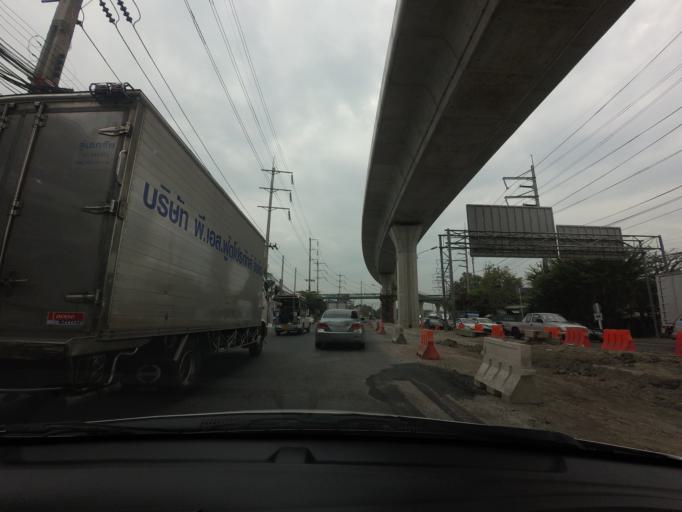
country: TH
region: Samut Prakan
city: Samut Prakan
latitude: 13.5912
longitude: 100.6094
